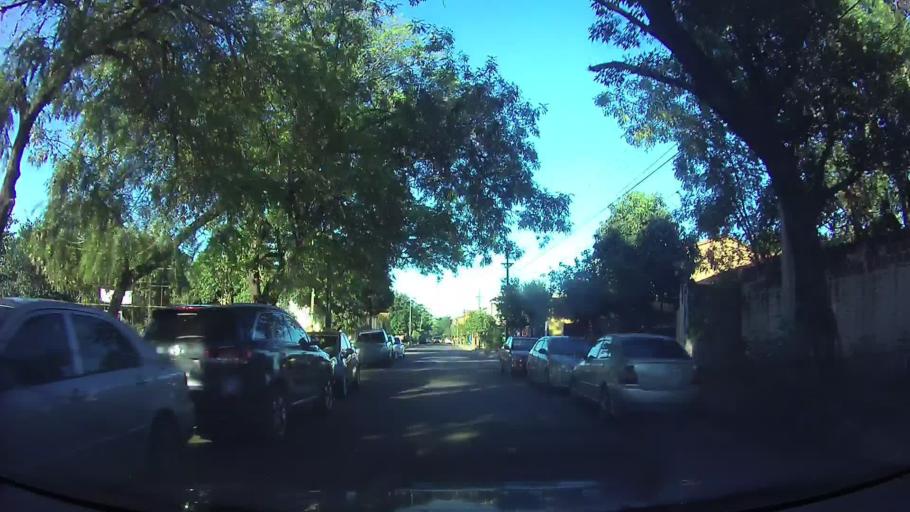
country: PY
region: Central
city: Fernando de la Mora
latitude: -25.3231
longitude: -57.5656
